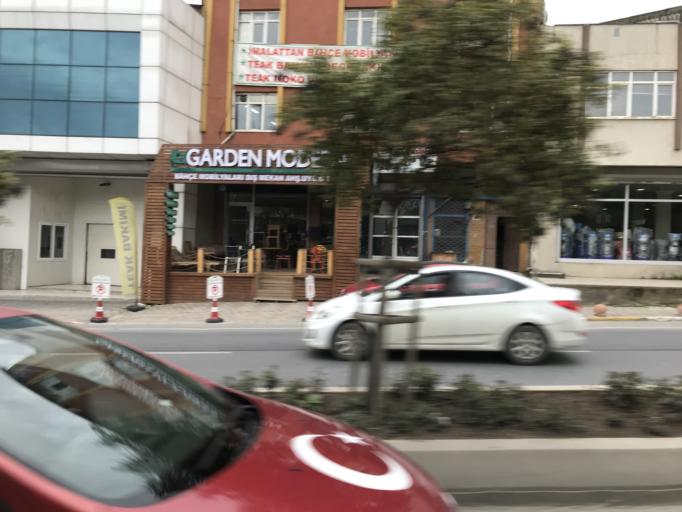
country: TR
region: Istanbul
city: Umraniye
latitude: 41.0123
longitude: 29.1645
